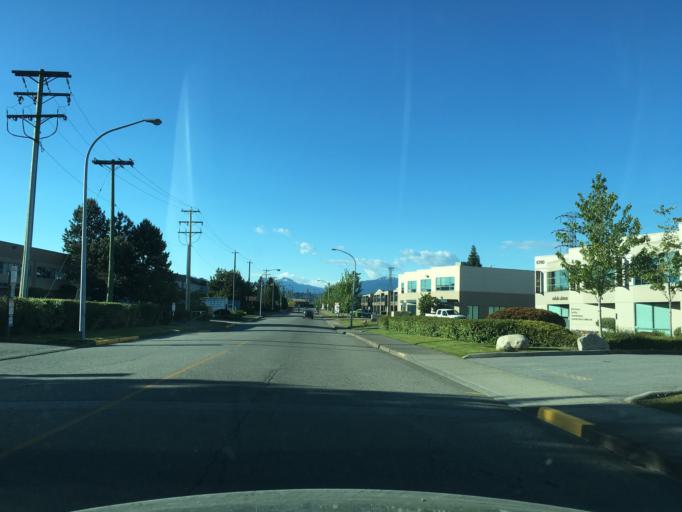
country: CA
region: British Columbia
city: Delta
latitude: 49.1649
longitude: -122.9897
